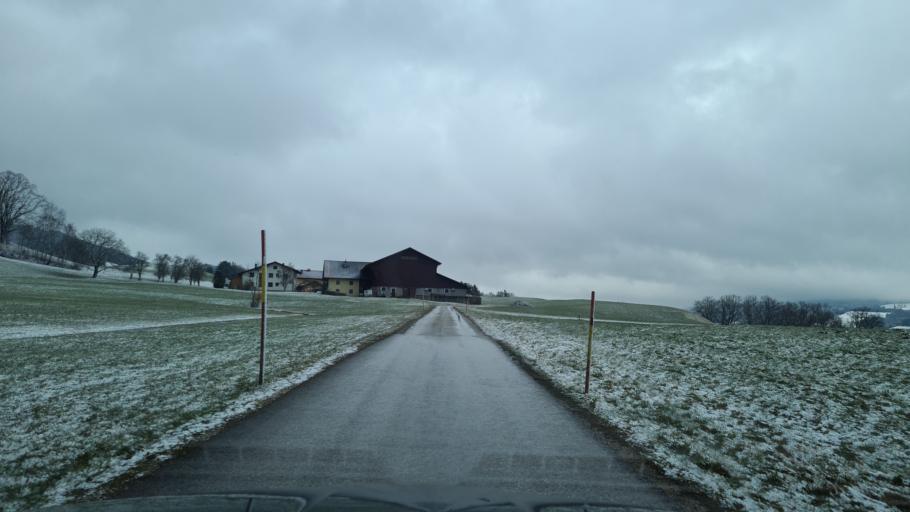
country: AT
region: Upper Austria
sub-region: Politischer Bezirk Vocklabruck
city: Oberhofen am Irrsee
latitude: 47.9531
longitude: 13.3125
